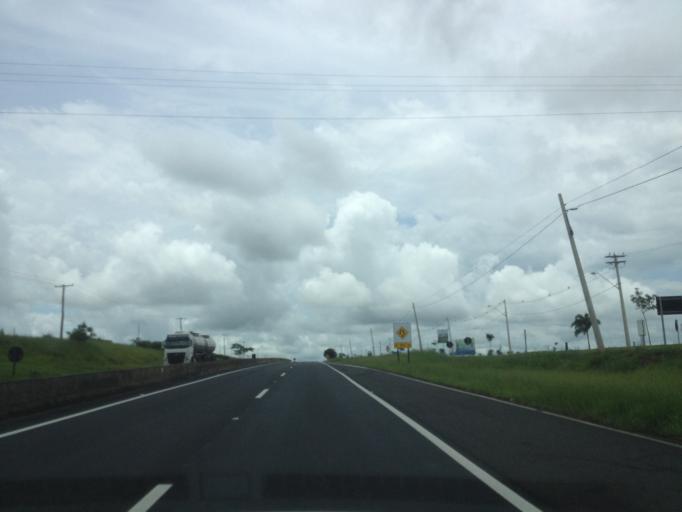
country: BR
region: Sao Paulo
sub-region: Marilia
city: Marilia
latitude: -22.2544
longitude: -49.9897
